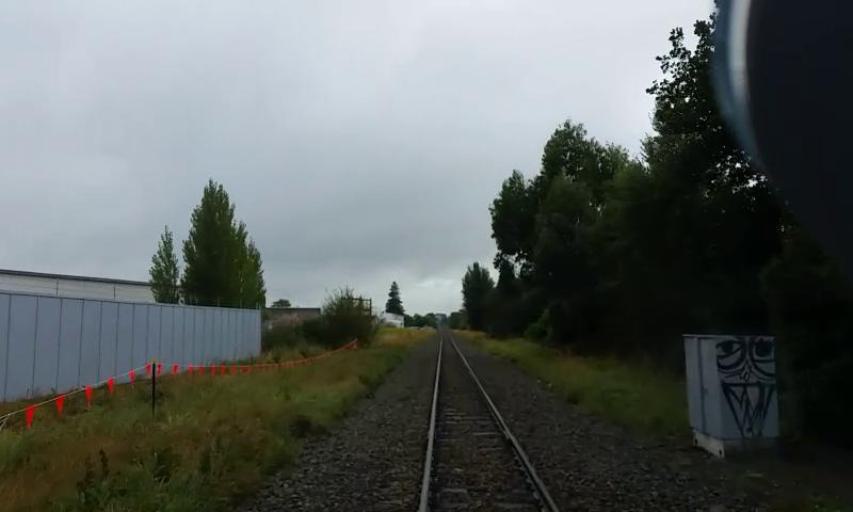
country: NZ
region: Canterbury
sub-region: Christchurch City
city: Christchurch
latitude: -43.5339
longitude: 172.6094
